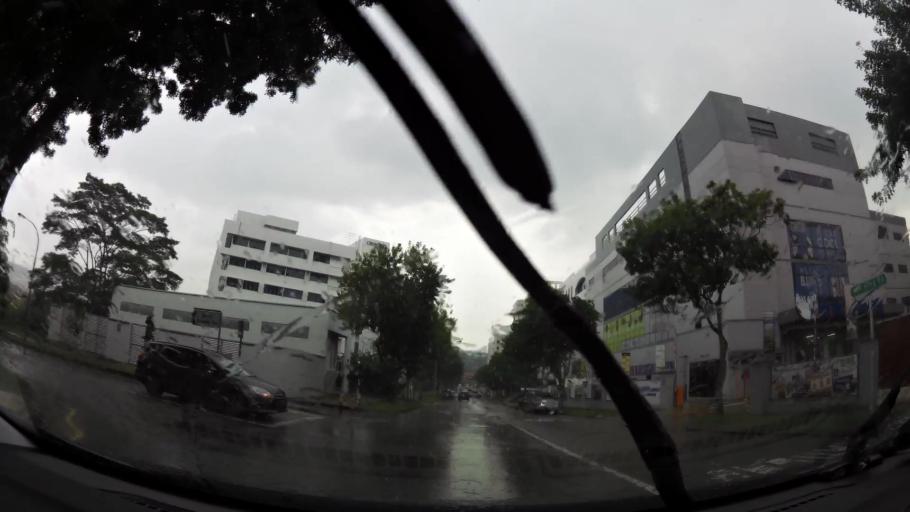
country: SG
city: Singapore
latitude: 1.3380
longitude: 103.8833
